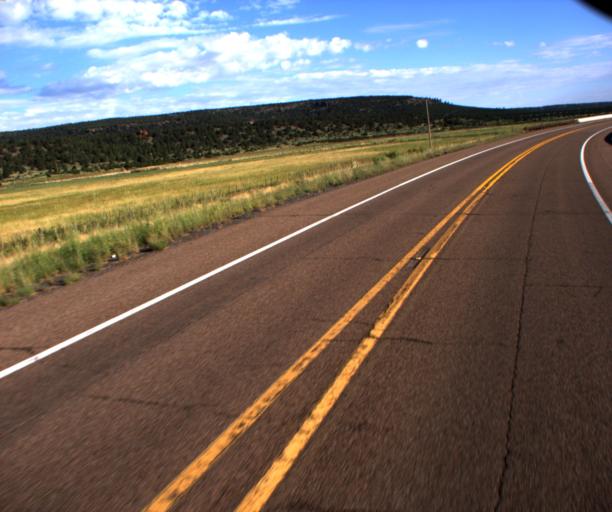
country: US
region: Arizona
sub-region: Apache County
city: Eagar
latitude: 33.9531
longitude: -109.2113
